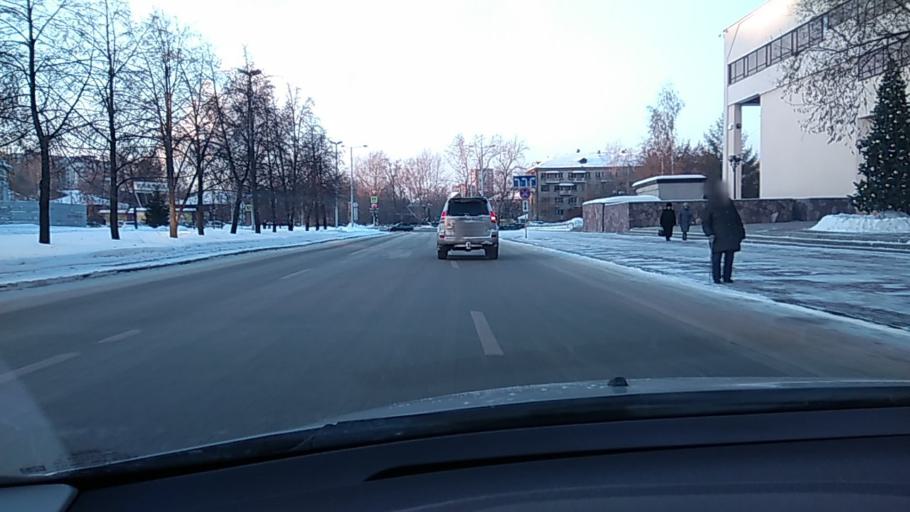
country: RU
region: Sverdlovsk
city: Yekaterinburg
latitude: 56.8451
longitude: 60.5884
